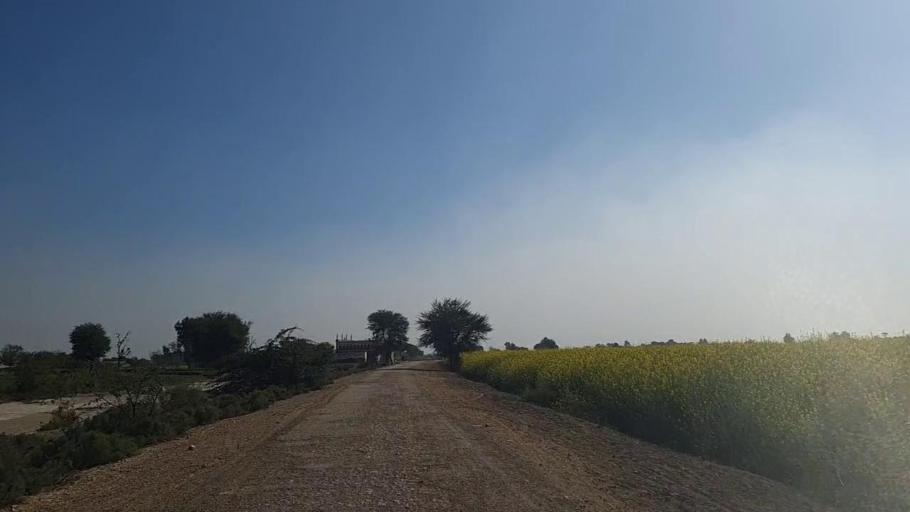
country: PK
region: Sindh
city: Shahpur Chakar
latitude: 26.2036
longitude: 68.6130
